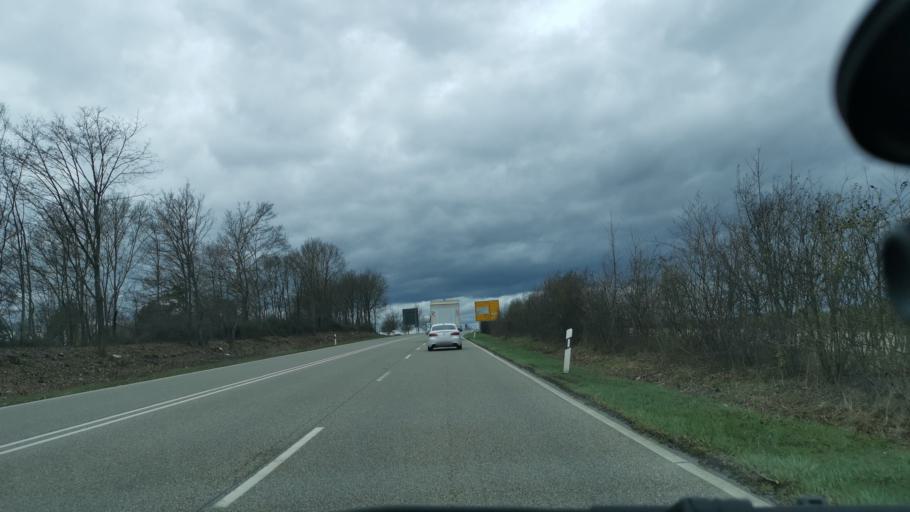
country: DE
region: Baden-Wuerttemberg
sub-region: Regierungsbezirk Stuttgart
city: Schwieberdingen
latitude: 48.8835
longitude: 9.0958
